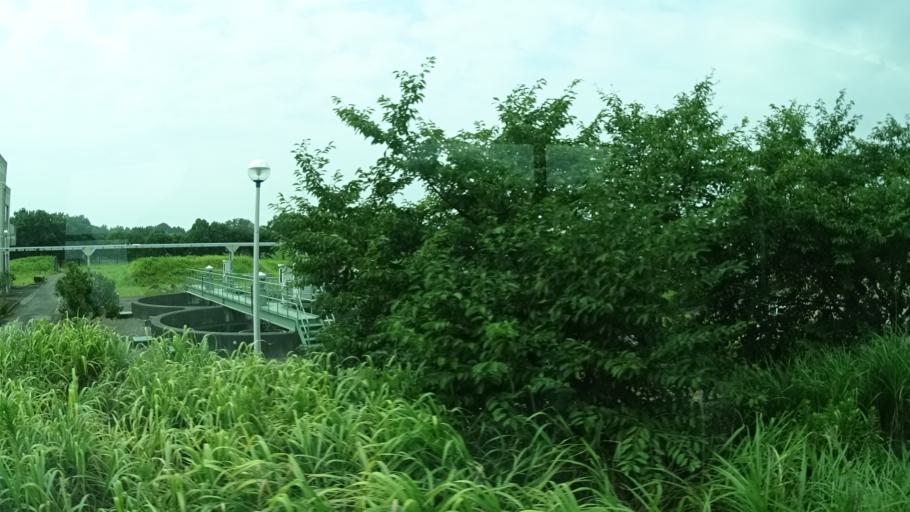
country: JP
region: Tochigi
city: Mashiko
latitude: 36.4581
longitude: 140.0853
